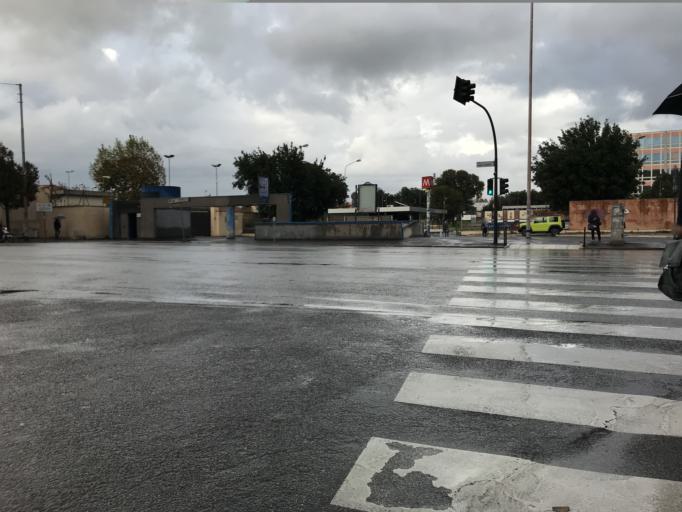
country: IT
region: Latium
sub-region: Citta metropolitana di Roma Capitale
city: Rome
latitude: 41.9060
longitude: 12.5054
